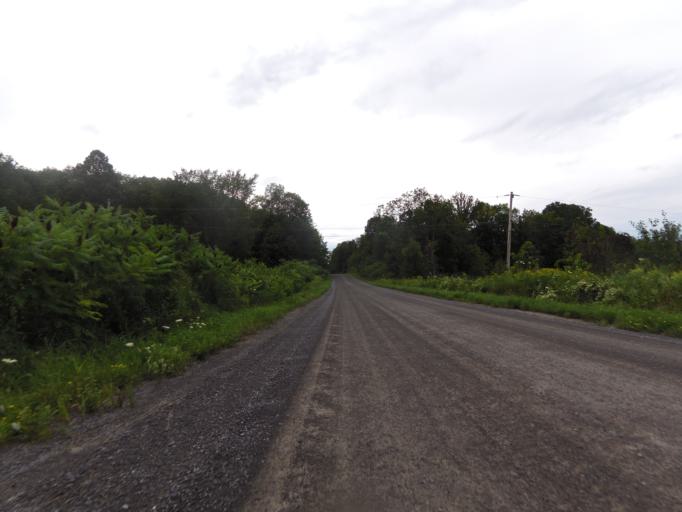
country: CA
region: Ontario
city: Carleton Place
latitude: 45.1642
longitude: -76.2727
